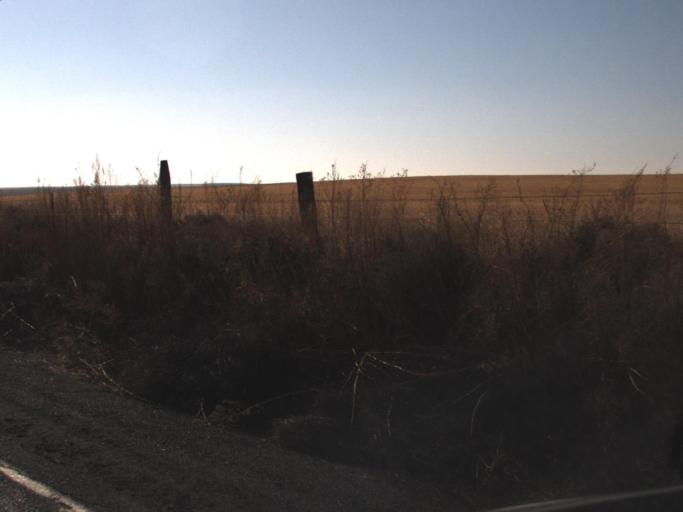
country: US
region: Washington
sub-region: Adams County
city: Ritzville
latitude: 47.0692
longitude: -118.6630
